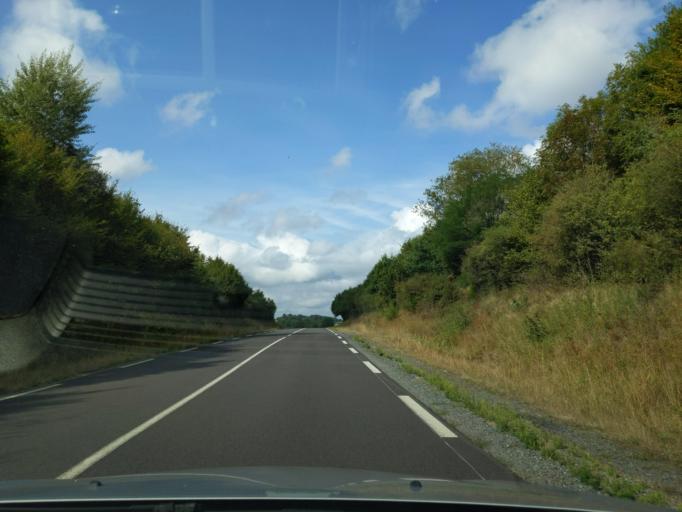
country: FR
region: Bourgogne
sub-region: Departement de la Nievre
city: Luzy
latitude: 46.8460
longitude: 4.0649
